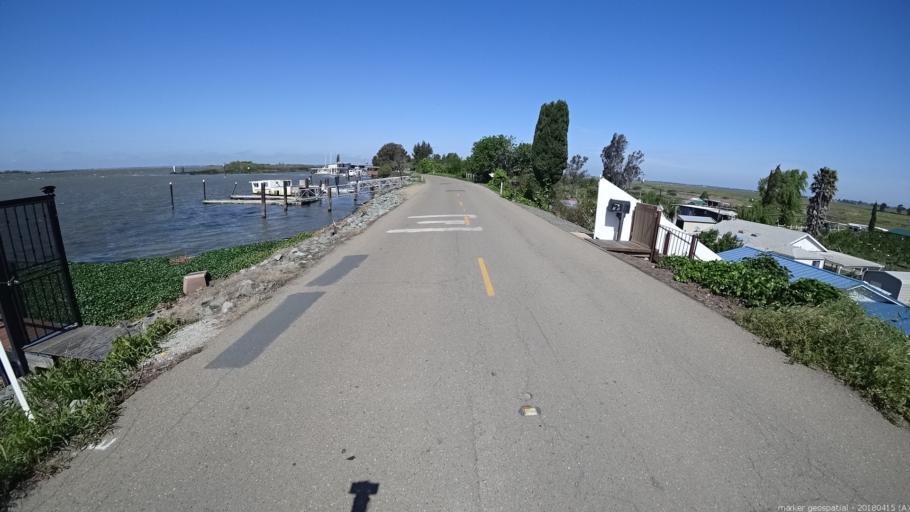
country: US
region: California
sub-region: Contra Costa County
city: Bethel Island
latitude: 38.1053
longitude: -121.5942
